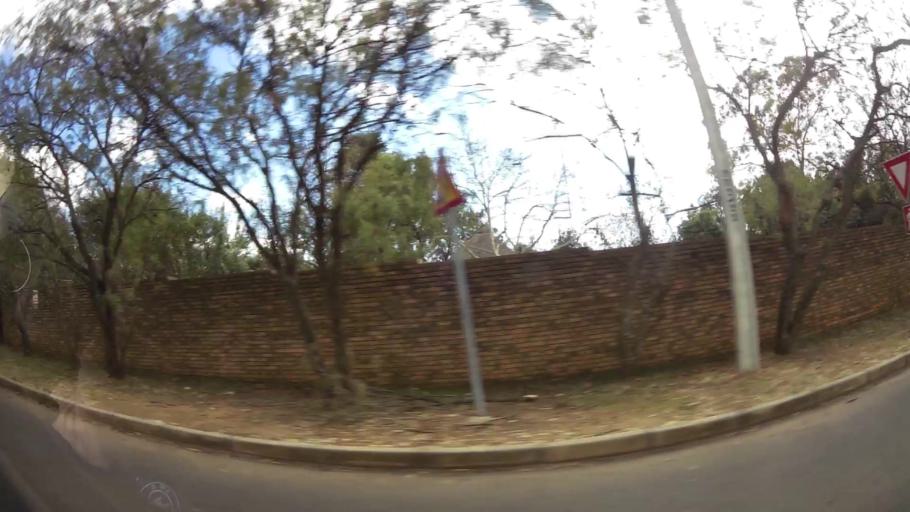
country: ZA
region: Gauteng
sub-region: West Rand District Municipality
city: Muldersdriseloop
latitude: -26.0933
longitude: 27.8613
